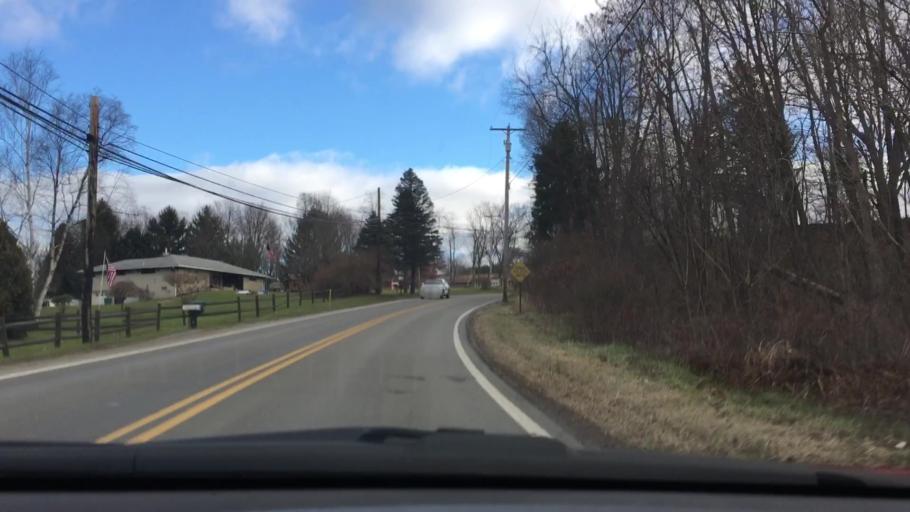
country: US
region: Pennsylvania
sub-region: Armstrong County
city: Orchard Hills
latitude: 40.6045
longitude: -79.4996
